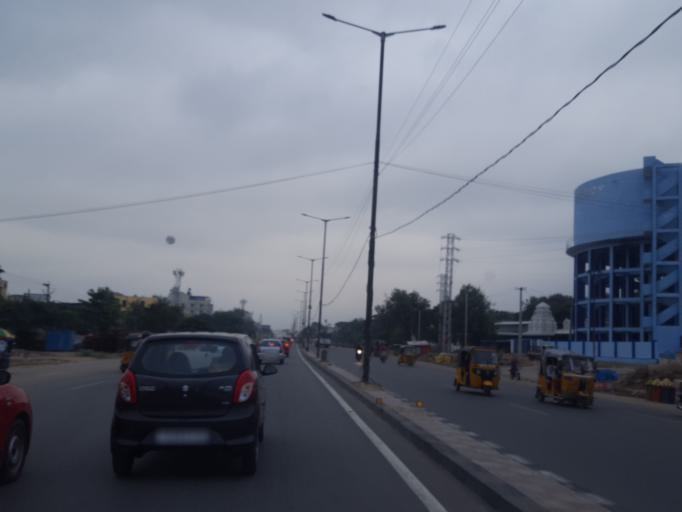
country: IN
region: Telangana
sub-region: Medak
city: Serilingampalle
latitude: 17.5074
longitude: 78.3034
